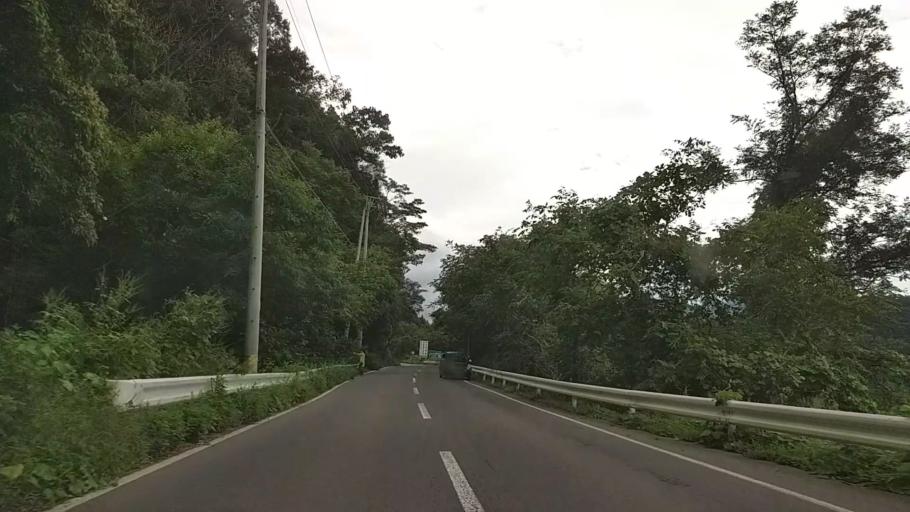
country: JP
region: Nagano
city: Nakano
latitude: 36.7792
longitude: 138.3301
